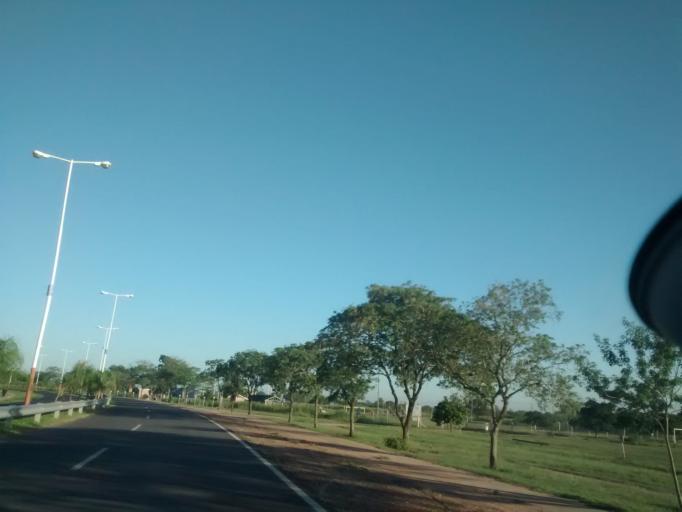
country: AR
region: Chaco
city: Fontana
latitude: -27.4421
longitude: -59.0272
